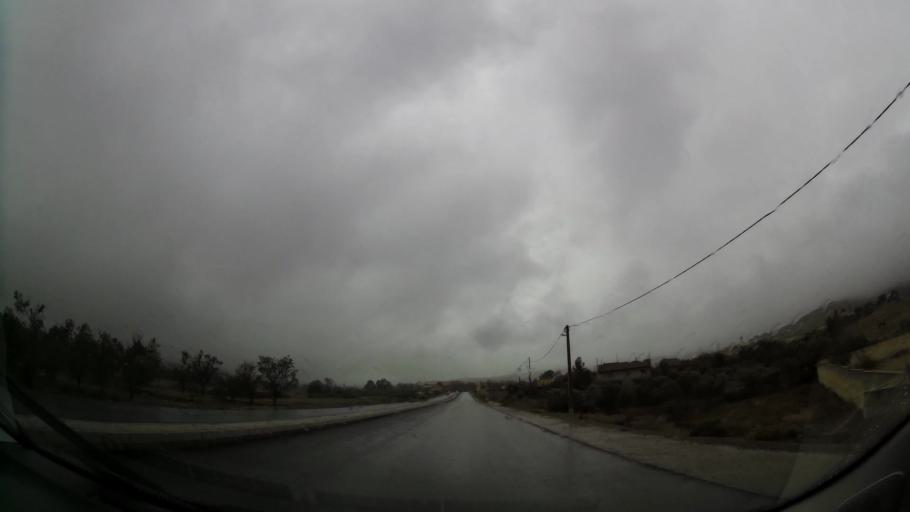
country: MA
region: Taza-Al Hoceima-Taounate
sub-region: Taza
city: Aknoul
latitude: 34.8137
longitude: -3.7322
